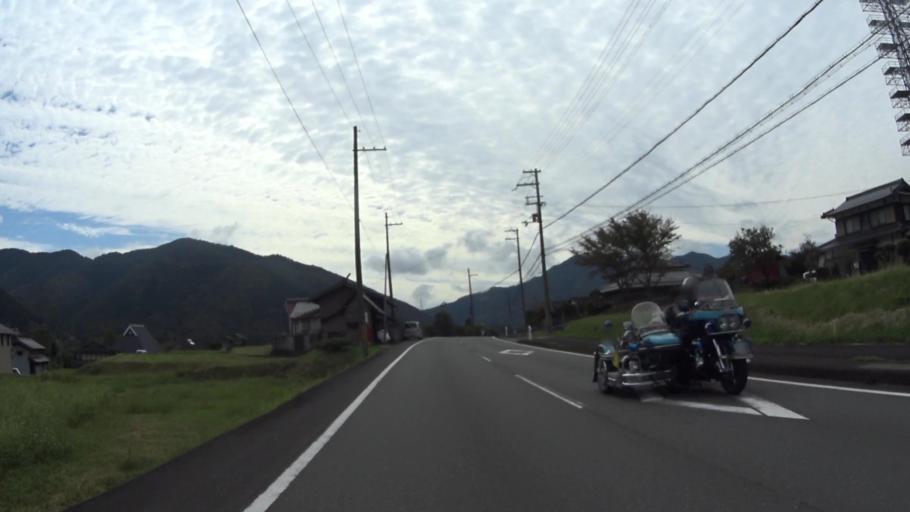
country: JP
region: Kyoto
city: Ayabe
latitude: 35.2533
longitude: 135.4224
